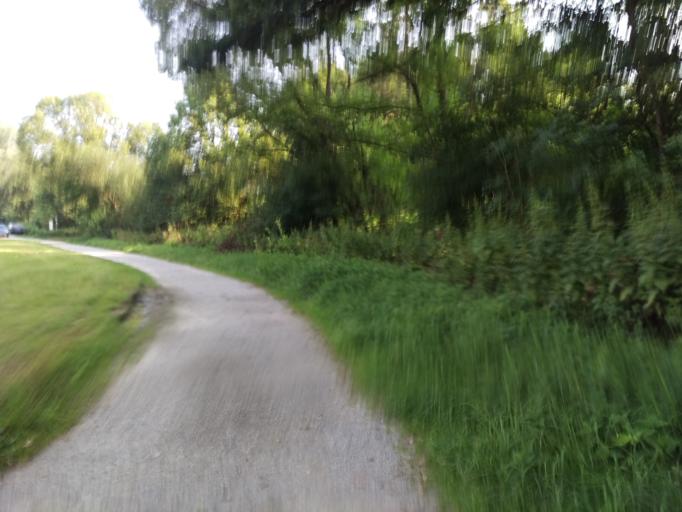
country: AT
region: Styria
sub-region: Politischer Bezirk Graz-Umgebung
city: Thal
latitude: 47.0609
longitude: 15.3648
